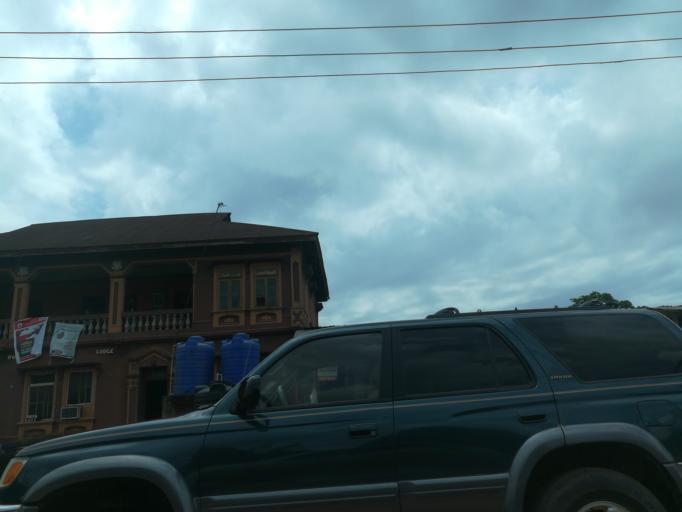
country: NG
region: Lagos
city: Ejirin
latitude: 6.6411
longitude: 3.7124
